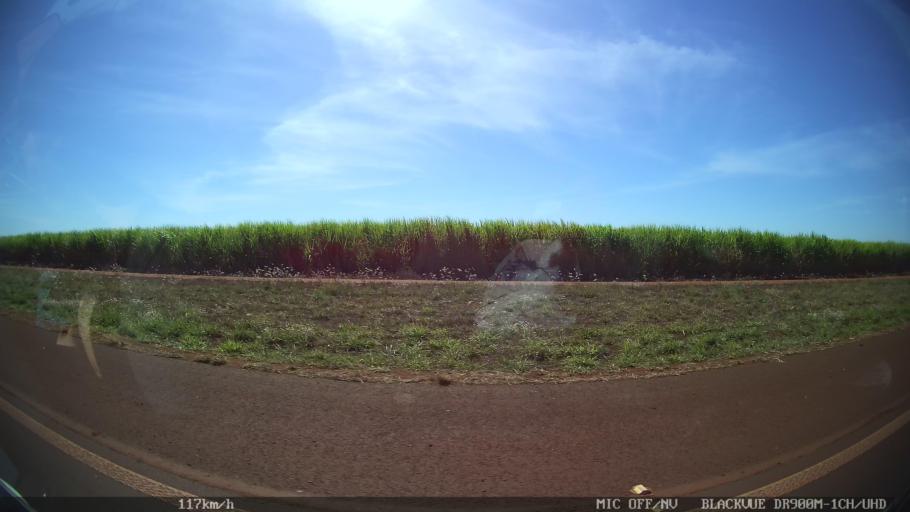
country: BR
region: Sao Paulo
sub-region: Guaira
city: Guaira
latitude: -20.4436
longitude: -48.3433
